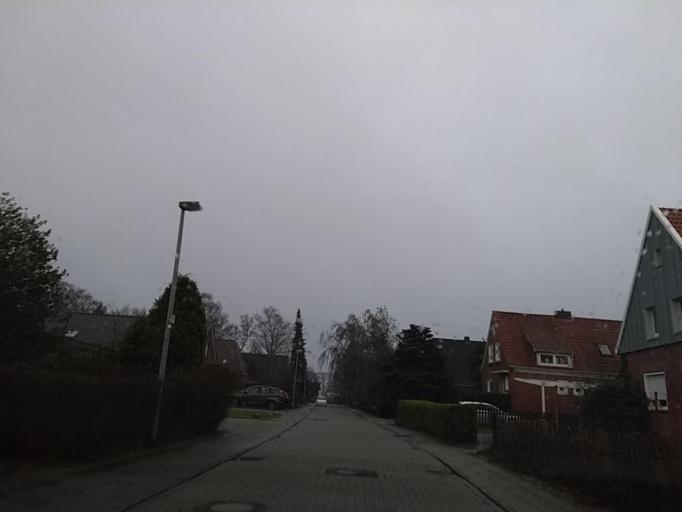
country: DE
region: Lower Saxony
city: Leer
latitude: 53.2346
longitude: 7.4836
